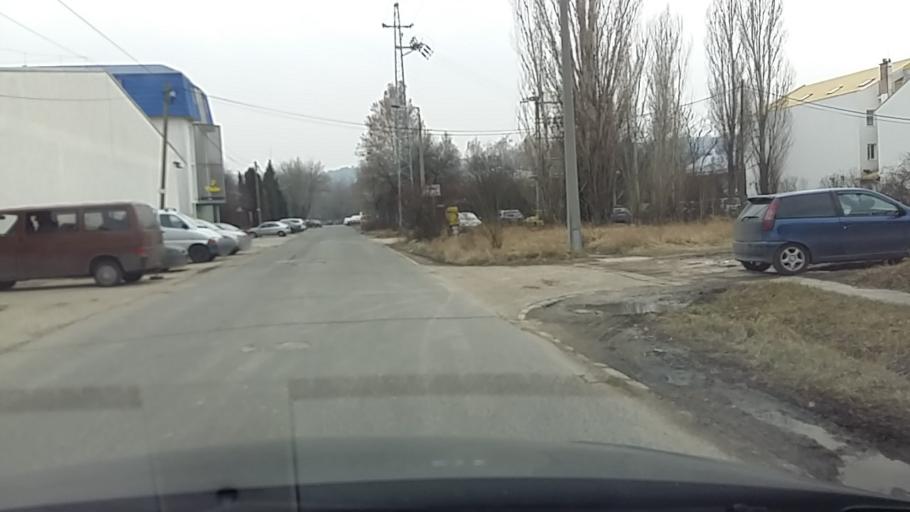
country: HU
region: Pest
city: Budaors
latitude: 47.4430
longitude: 18.9741
